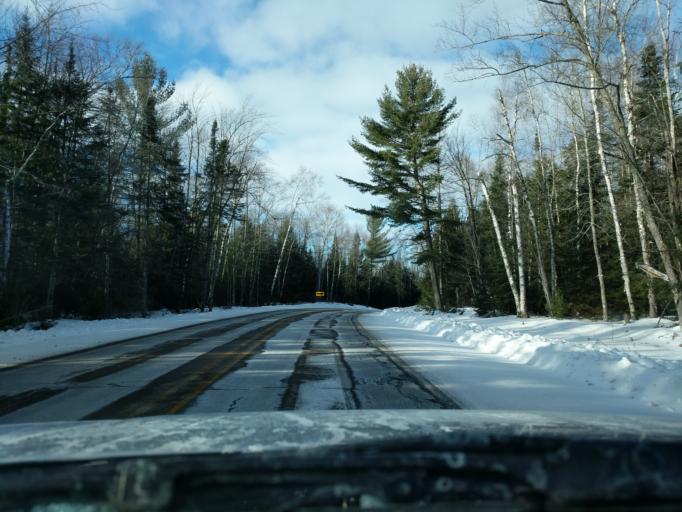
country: US
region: Wisconsin
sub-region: Vilas County
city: Eagle River
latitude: 45.7650
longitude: -89.0676
